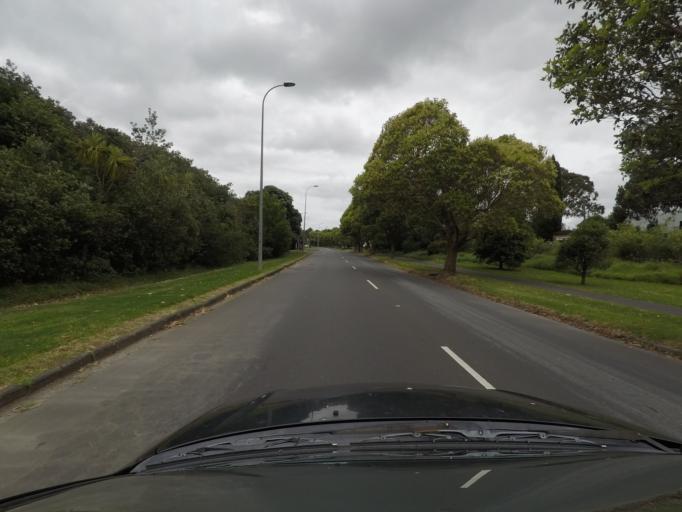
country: NZ
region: Auckland
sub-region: Auckland
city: Rosebank
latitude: -36.8594
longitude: 174.7142
